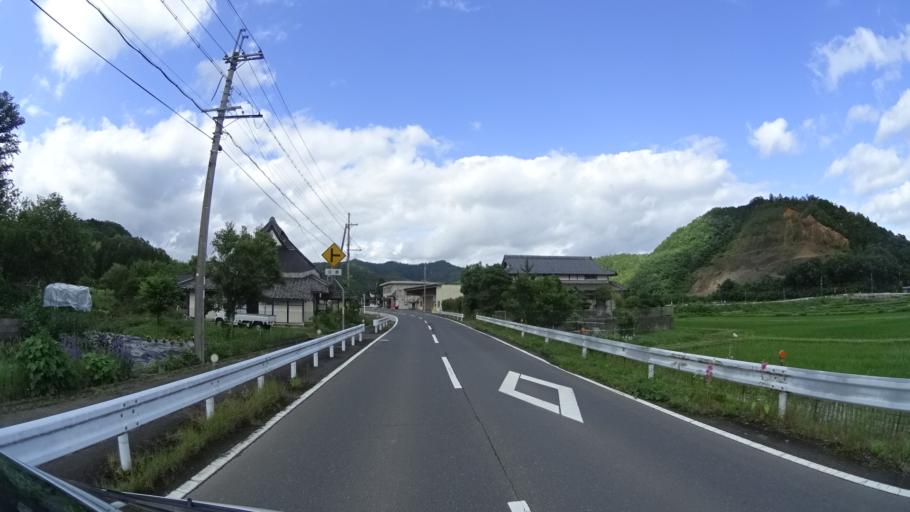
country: JP
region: Kyoto
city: Ayabe
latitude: 35.3636
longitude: 135.2378
